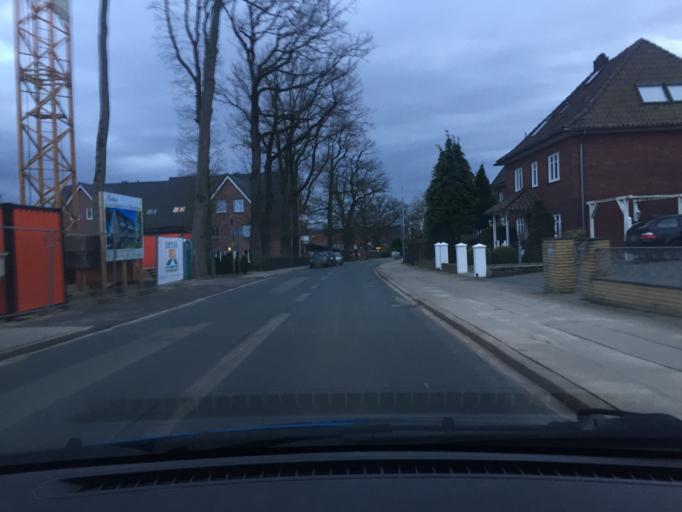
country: DE
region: Lower Saxony
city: Seevetal
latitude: 53.4346
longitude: 9.9062
